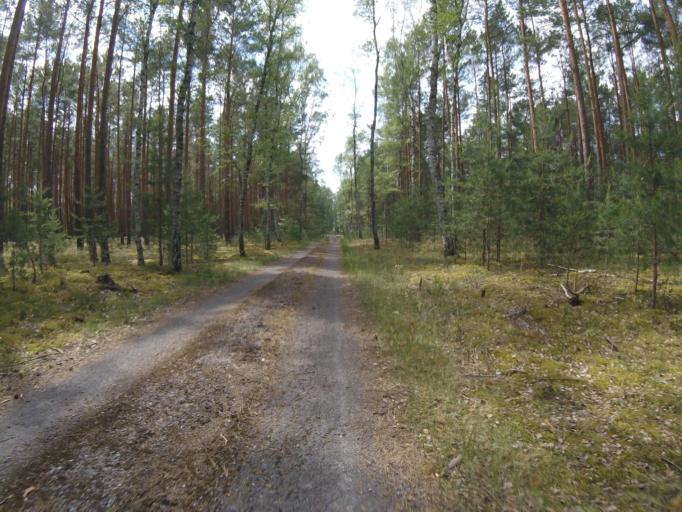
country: DE
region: Brandenburg
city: Halbe
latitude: 52.1218
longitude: 13.6699
